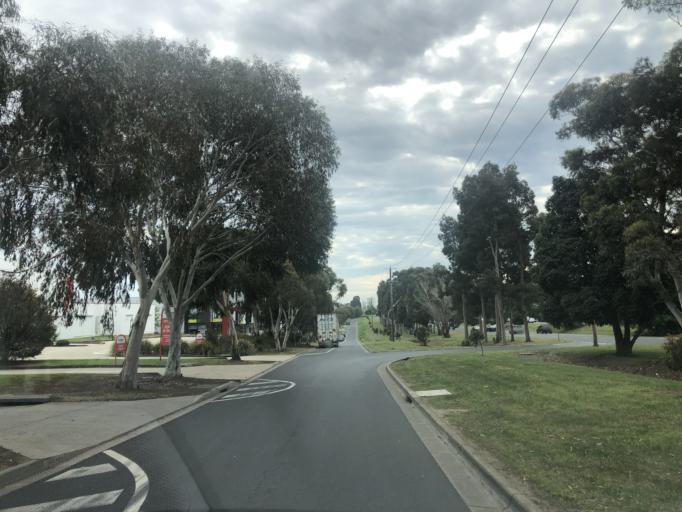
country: AU
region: Victoria
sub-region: Casey
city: Hallam
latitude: -38.0053
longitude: 145.2628
